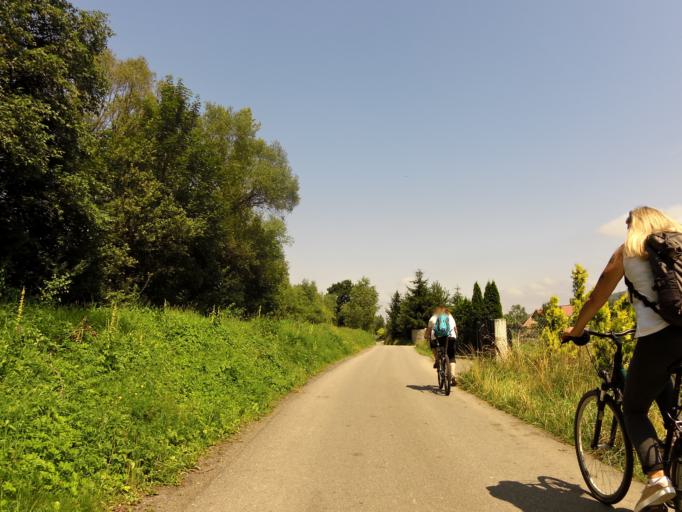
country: PL
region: Silesian Voivodeship
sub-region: Powiat zywiecki
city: Milowka
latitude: 49.5647
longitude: 19.0861
